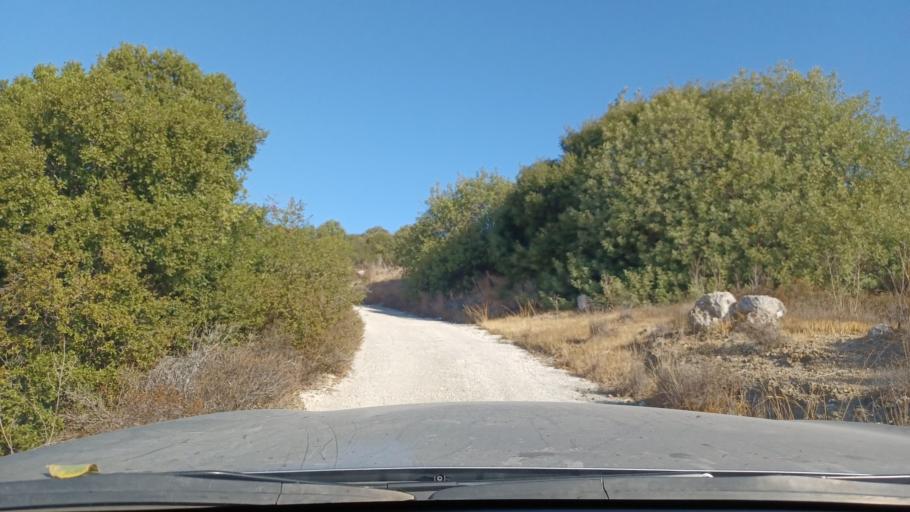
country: CY
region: Pafos
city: Polis
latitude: 35.0023
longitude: 32.4911
